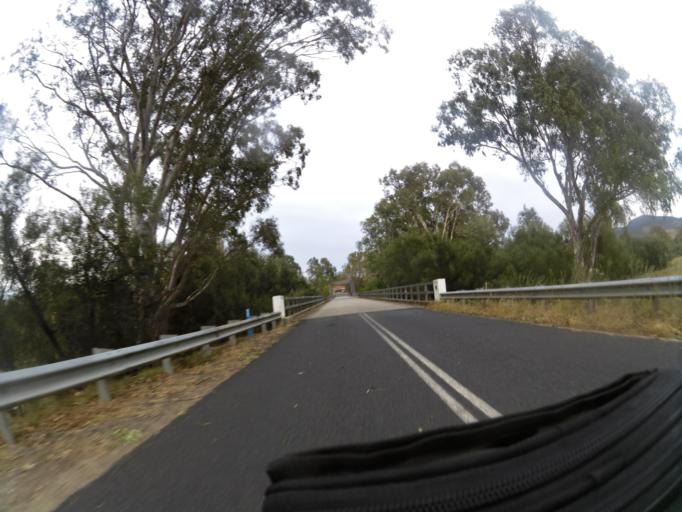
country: AU
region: New South Wales
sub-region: Greater Hume Shire
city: Holbrook
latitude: -36.0450
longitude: 147.9335
